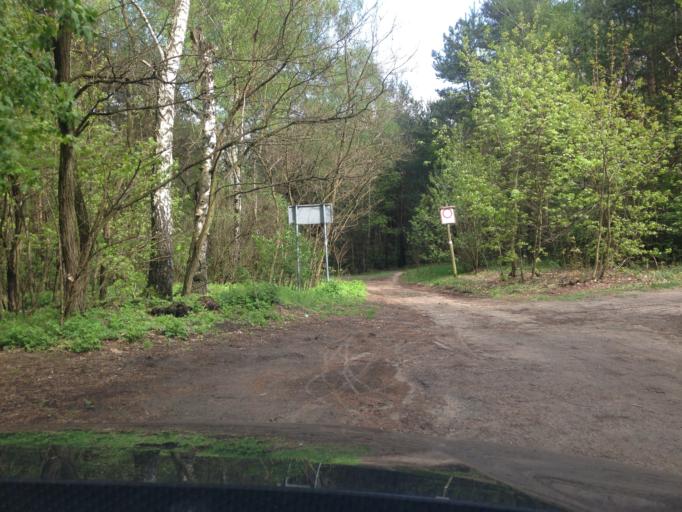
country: PL
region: Masovian Voivodeship
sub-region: Powiat warszawski zachodni
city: Izabelin
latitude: 52.3130
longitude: 20.8245
